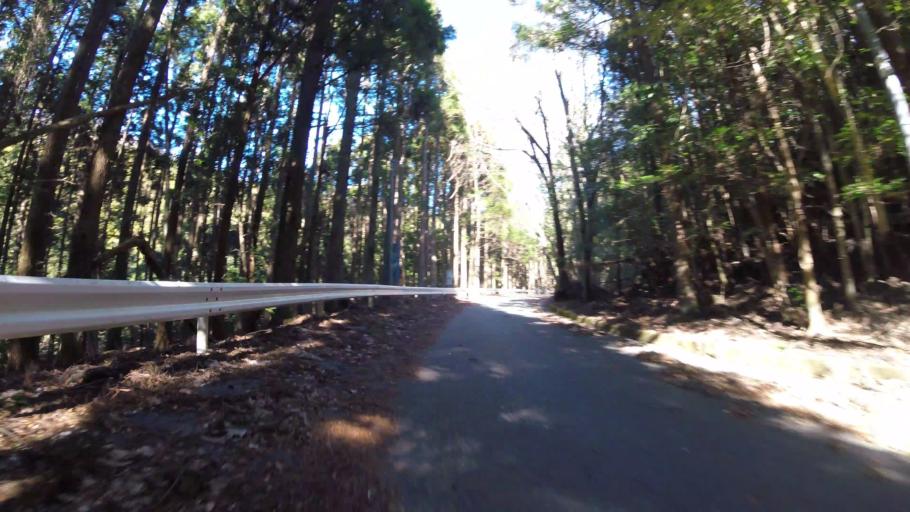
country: JP
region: Shizuoka
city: Ito
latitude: 34.8929
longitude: 138.9511
